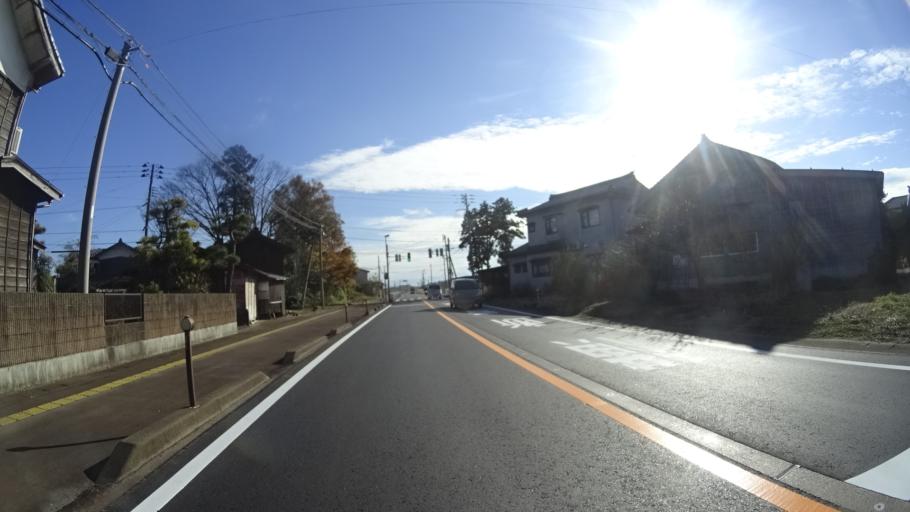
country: JP
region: Niigata
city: Mitsuke
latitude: 37.5544
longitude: 138.8567
